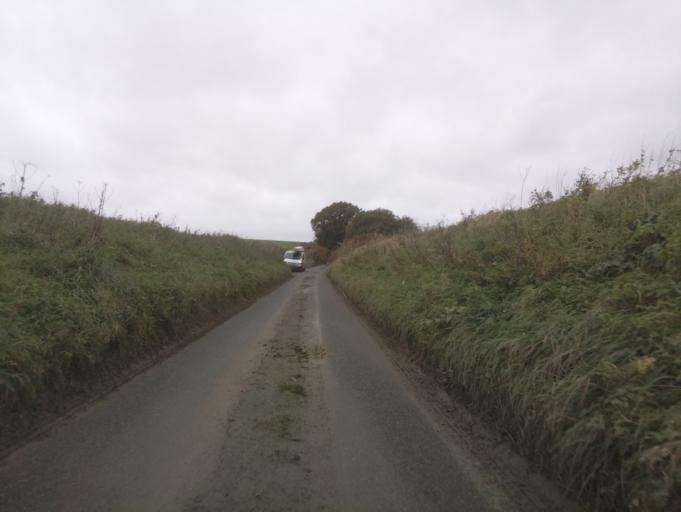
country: GB
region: England
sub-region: Somerset
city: South Petherton
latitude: 50.9452
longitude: -2.8578
